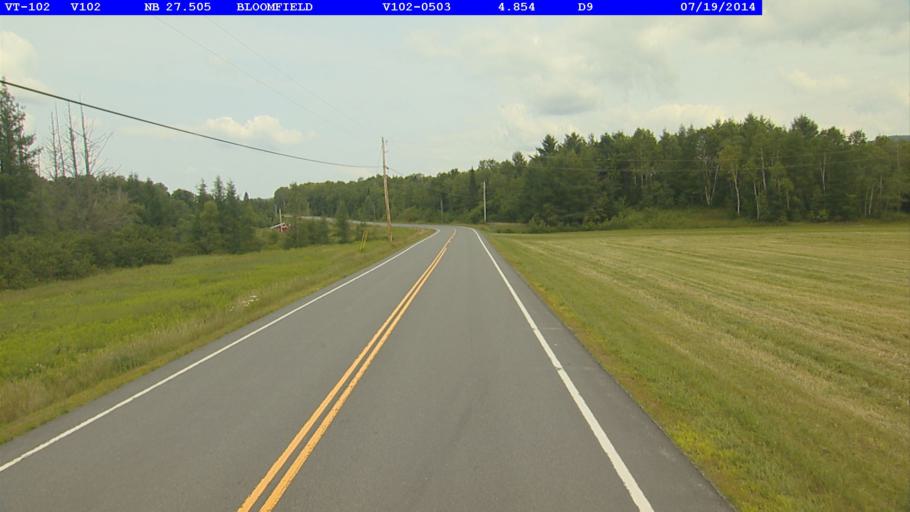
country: US
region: New Hampshire
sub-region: Coos County
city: Colebrook
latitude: 44.8006
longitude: -71.5741
